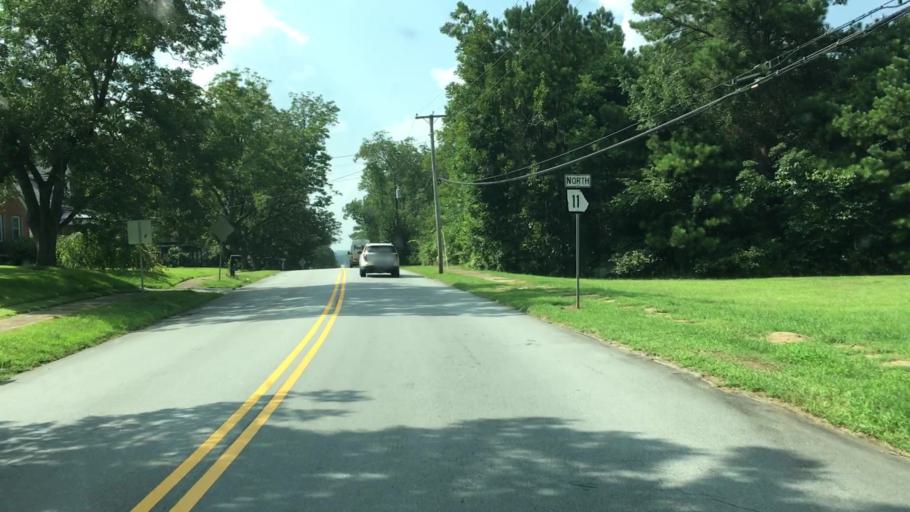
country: US
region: Georgia
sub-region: Jasper County
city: Monticello
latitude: 33.3119
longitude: -83.6870
